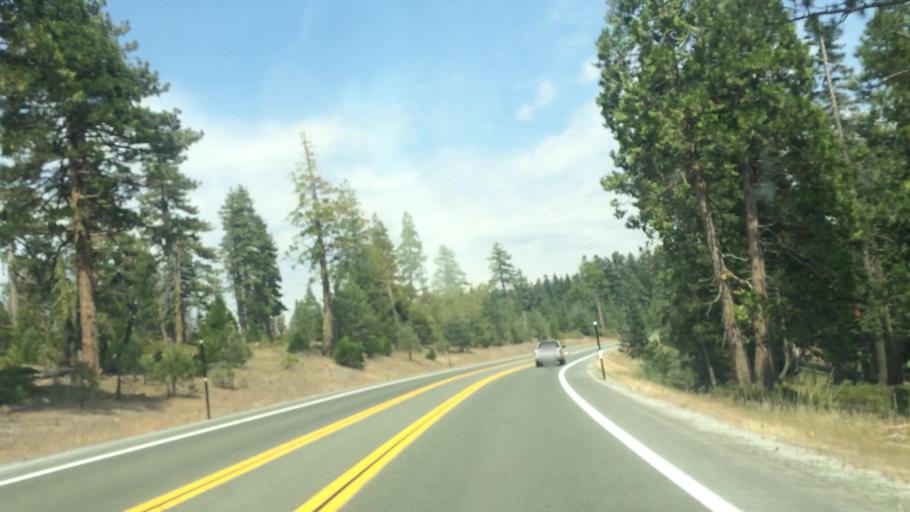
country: US
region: California
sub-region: Calaveras County
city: Arnold
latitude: 38.5588
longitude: -120.2812
